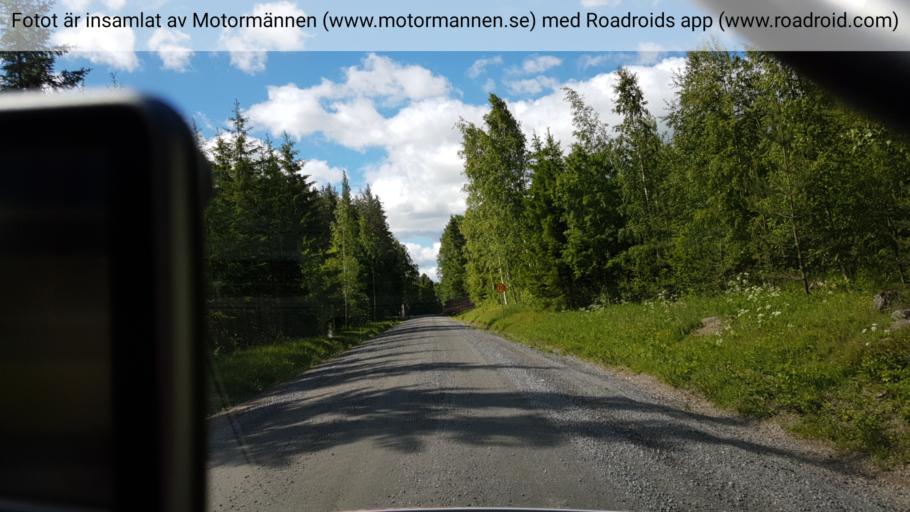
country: SE
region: Gaevleborg
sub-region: Hudiksvalls Kommun
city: Sorforsa
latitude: 61.6540
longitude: 16.9257
